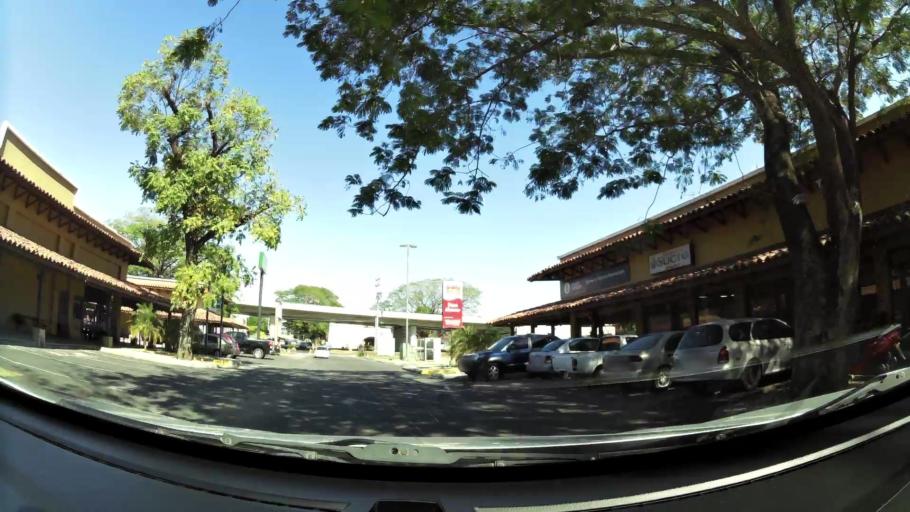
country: CR
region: Guanacaste
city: Liberia
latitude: 10.6255
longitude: -85.4438
